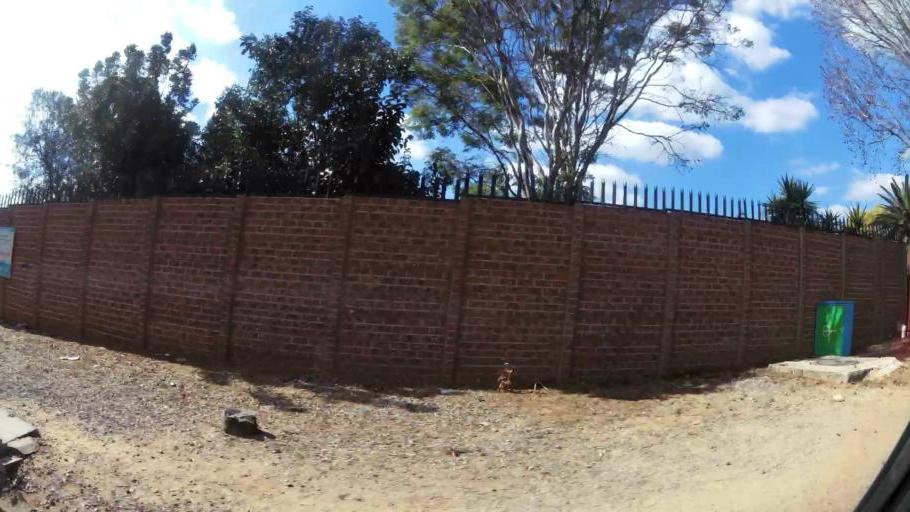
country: ZA
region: Gauteng
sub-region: City of Johannesburg Metropolitan Municipality
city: Roodepoort
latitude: -26.0749
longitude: 27.9693
